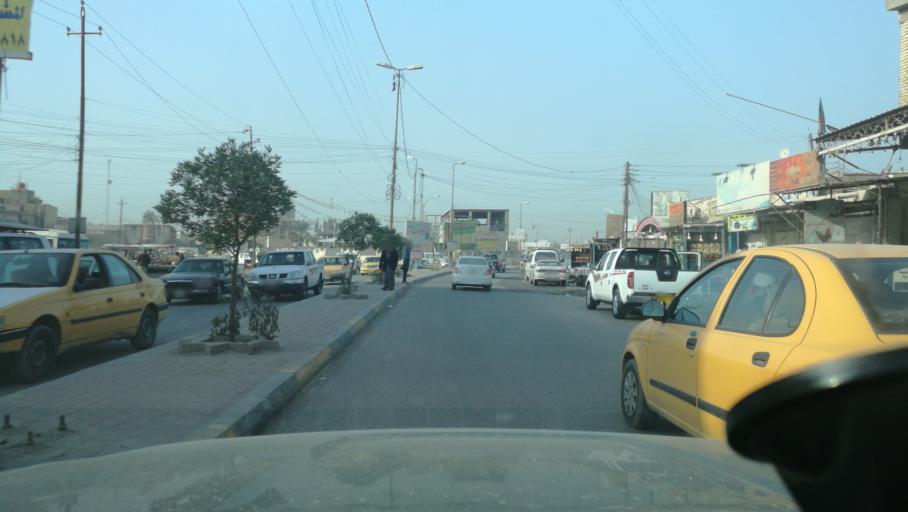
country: IQ
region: Basra Governorate
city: Al Basrah al Qadimah
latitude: 30.4949
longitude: 47.8202
